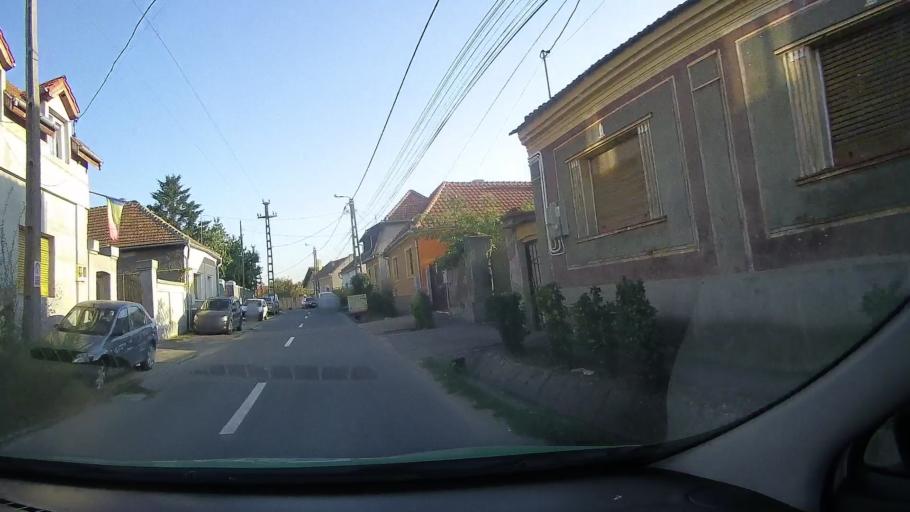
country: RO
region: Bihor
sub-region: Comuna Biharea
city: Oradea
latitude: 47.0998
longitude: 21.8972
